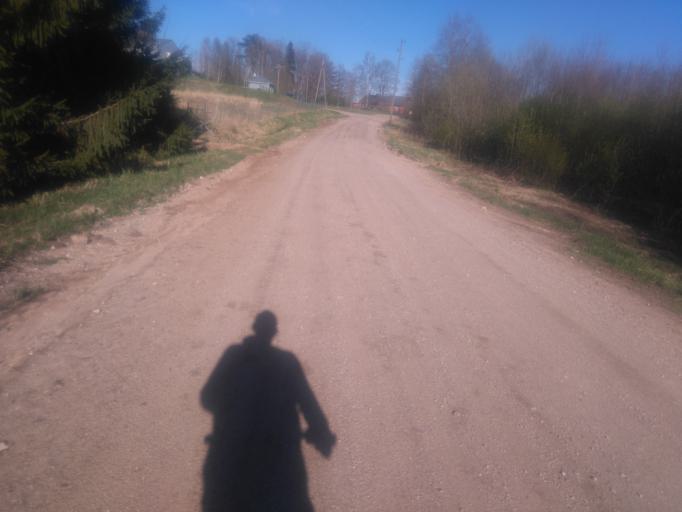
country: LV
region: Vecpiebalga
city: Vecpiebalga
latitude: 57.0192
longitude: 25.8475
